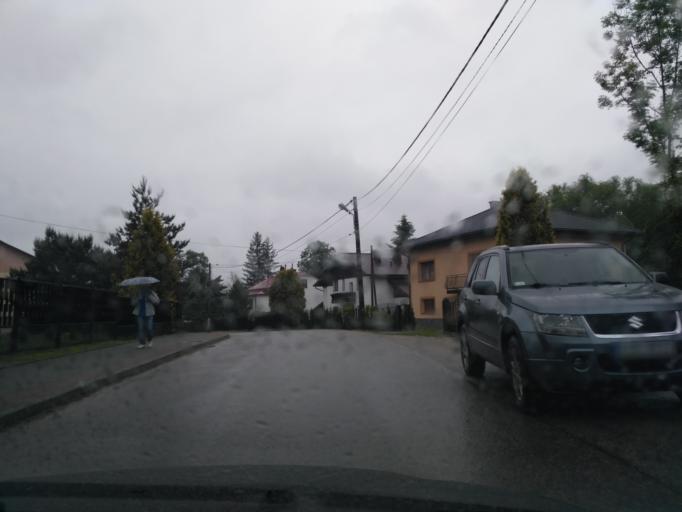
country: PL
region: Lesser Poland Voivodeship
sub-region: Powiat gorlicki
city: Gorlice
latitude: 49.6672
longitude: 21.1416
